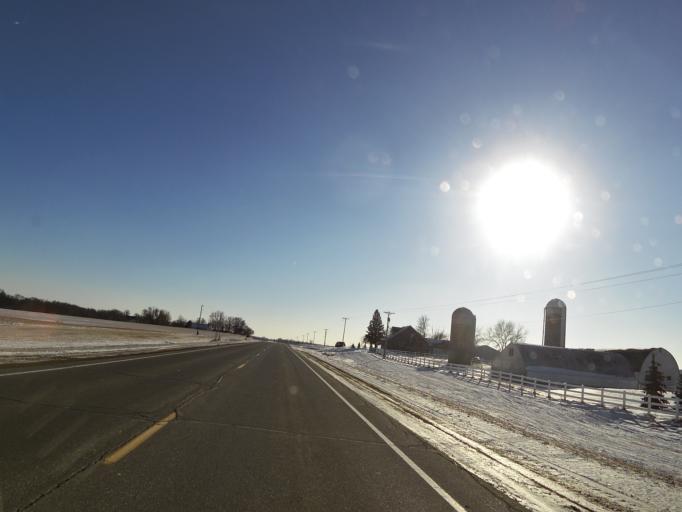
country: US
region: Minnesota
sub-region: Scott County
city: Prior Lake
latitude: 44.6835
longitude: -93.5011
